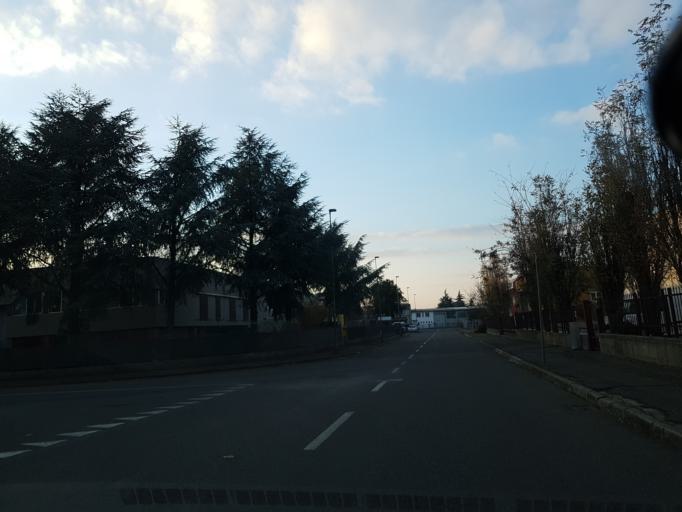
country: IT
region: Piedmont
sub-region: Provincia di Alessandria
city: Novi Ligure
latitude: 44.7537
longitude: 8.8115
